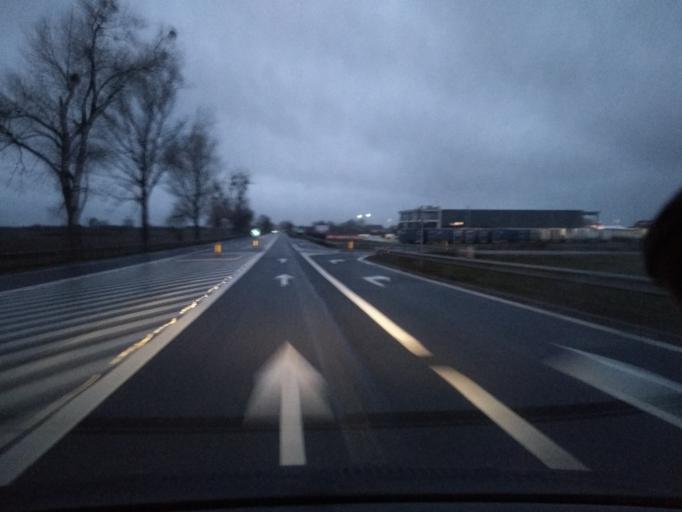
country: PL
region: Lower Silesian Voivodeship
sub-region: Powiat sredzki
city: Szczepanow
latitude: 51.1645
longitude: 16.6480
